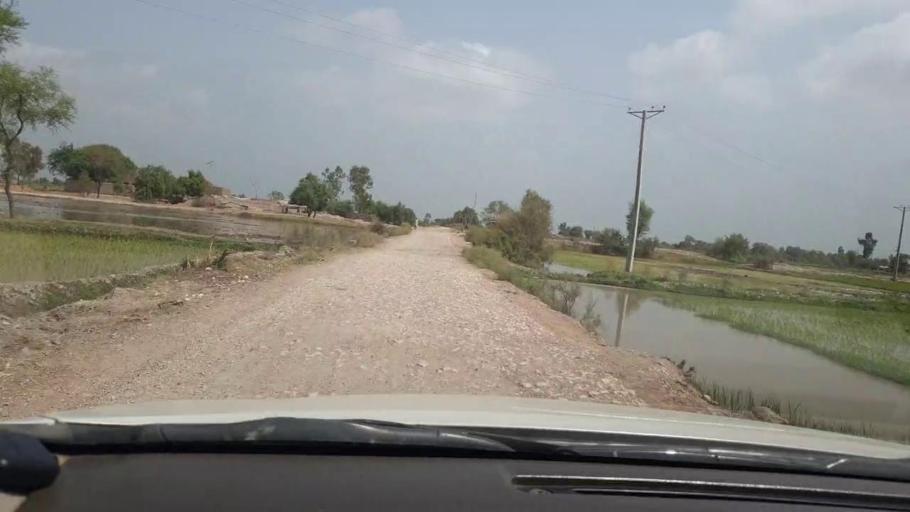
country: PK
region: Sindh
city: Garhi Yasin
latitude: 28.0148
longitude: 68.5285
